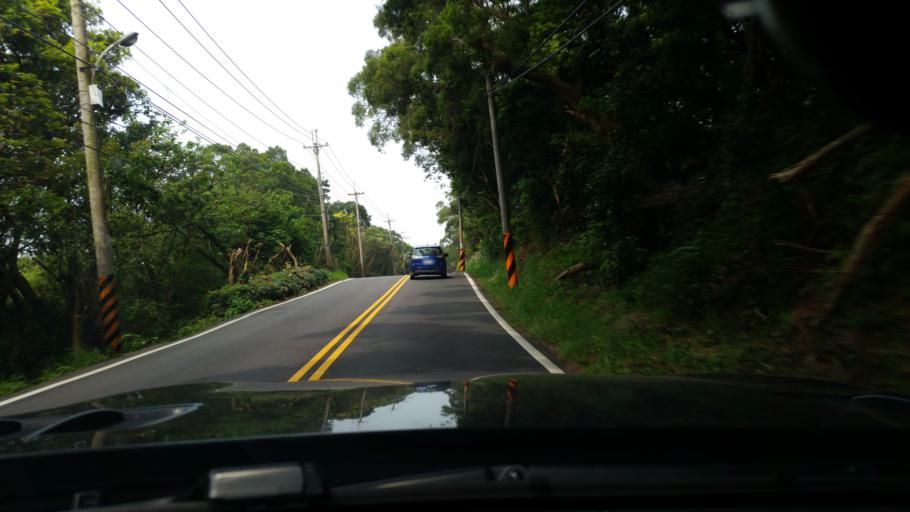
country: TW
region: Taiwan
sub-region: Taoyuan
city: Taoyuan
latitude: 25.0587
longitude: 121.3258
